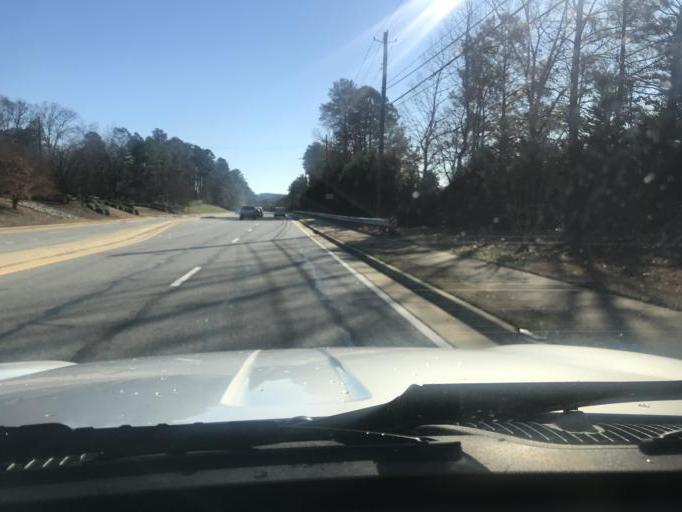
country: US
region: Georgia
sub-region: Gwinnett County
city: Lawrenceville
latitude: 33.9710
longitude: -84.0473
